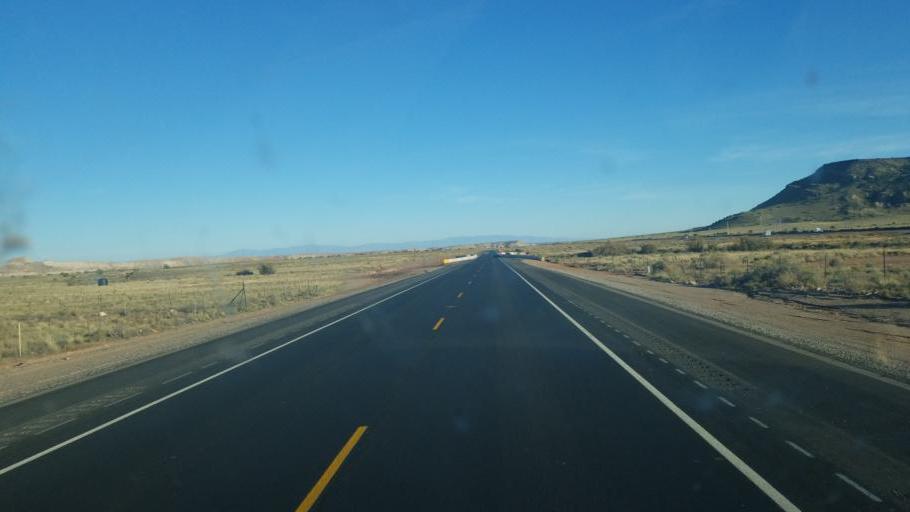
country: US
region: New Mexico
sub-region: Cibola County
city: Laguna
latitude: 34.9375
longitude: -107.1404
